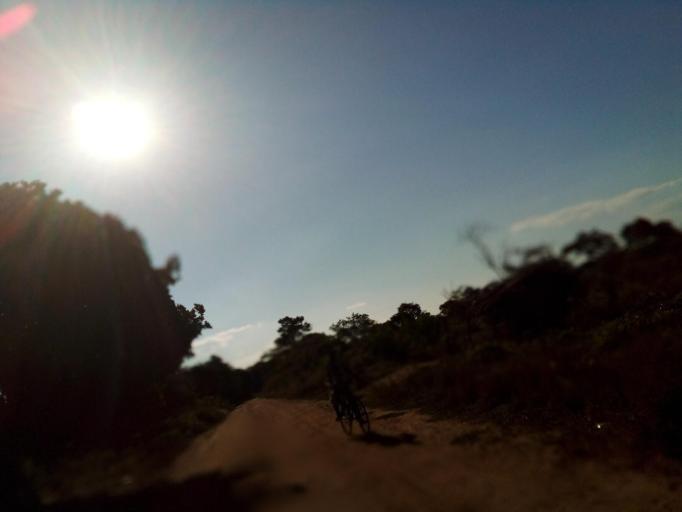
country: MZ
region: Zambezia
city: Quelimane
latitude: -17.4826
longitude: 36.5450
